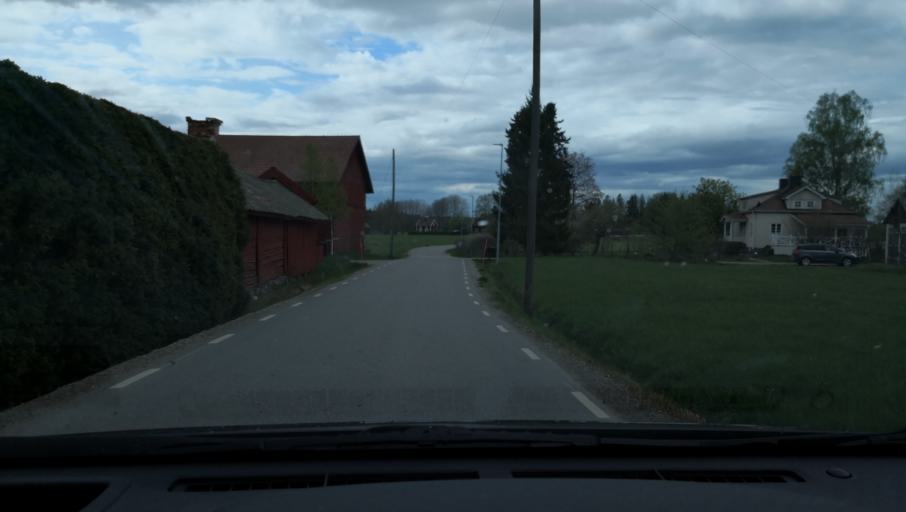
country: SE
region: Dalarna
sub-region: Avesta Kommun
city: Avesta
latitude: 60.0225
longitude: 16.2689
